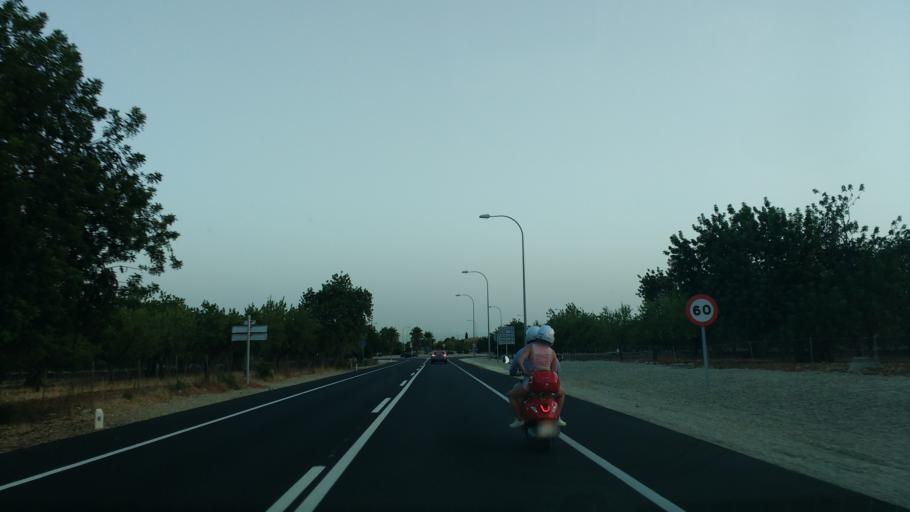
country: ES
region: Balearic Islands
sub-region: Illes Balears
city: Bunyola
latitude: 39.6699
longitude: 2.6772
